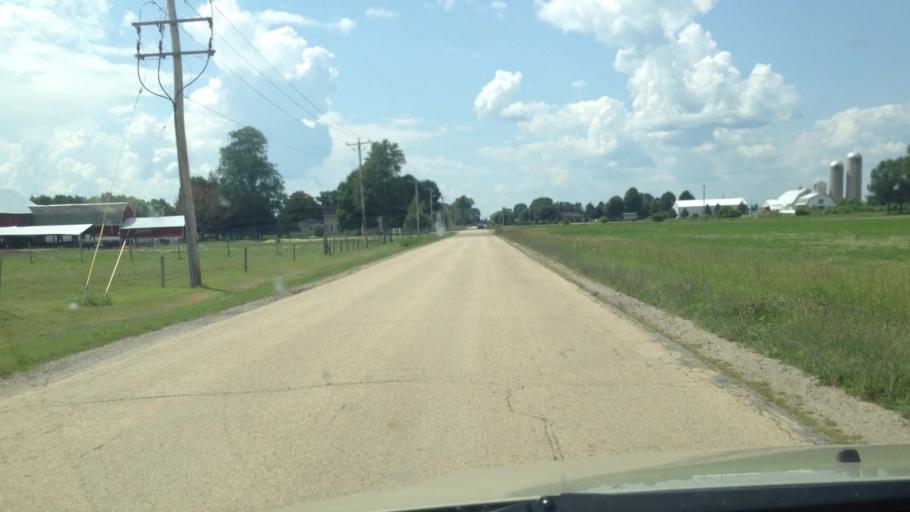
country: US
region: Wisconsin
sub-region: Brown County
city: Pulaski
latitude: 44.6567
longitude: -88.2536
